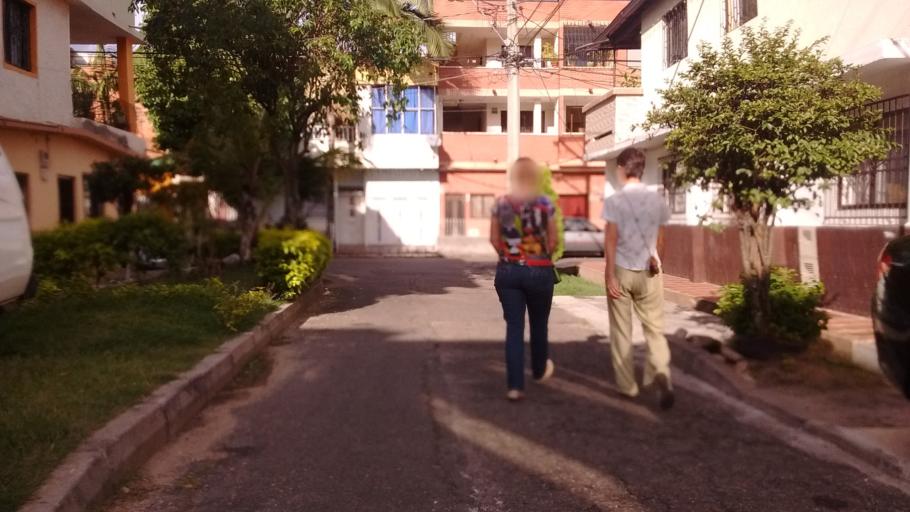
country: CO
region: Antioquia
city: Medellin
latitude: 6.2566
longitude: -75.6077
